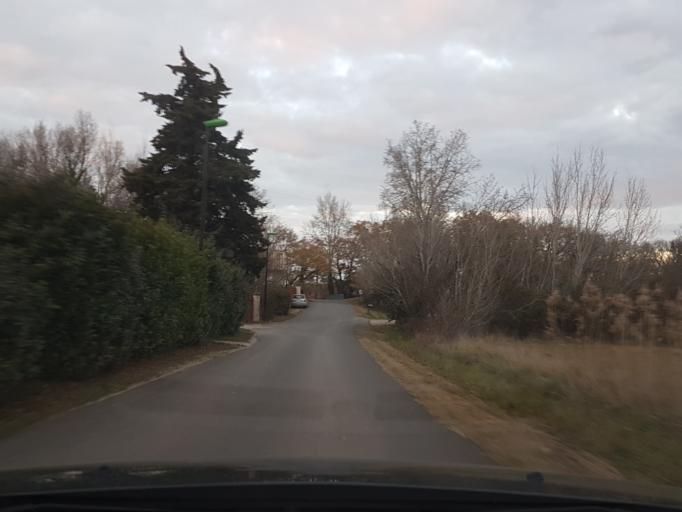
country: FR
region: Provence-Alpes-Cote d'Azur
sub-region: Departement du Vaucluse
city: Loriol-du-Comtat
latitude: 44.0791
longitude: 4.9996
